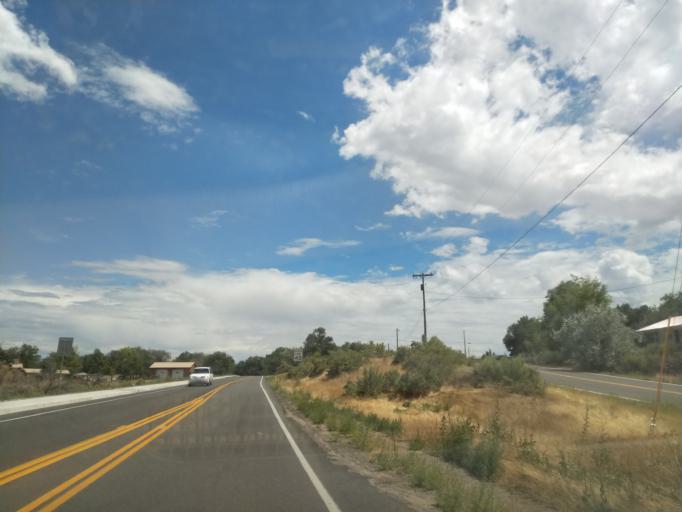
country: US
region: Colorado
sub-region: Mesa County
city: Redlands
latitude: 39.0771
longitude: -108.6328
